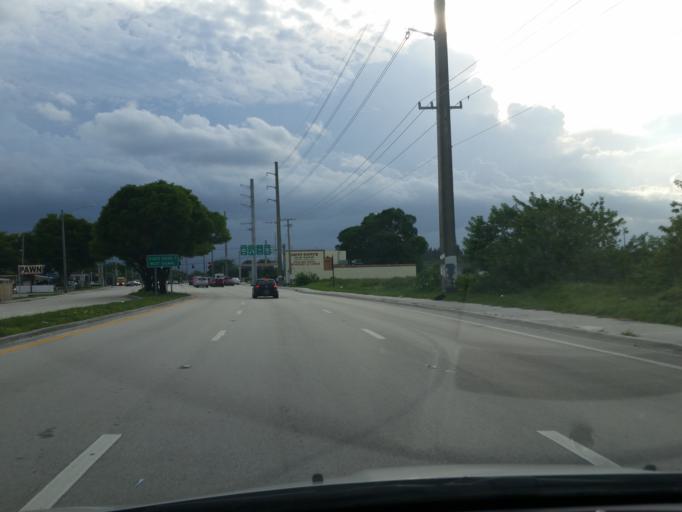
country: US
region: Florida
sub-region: Broward County
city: Davie
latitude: 26.0629
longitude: -80.2055
